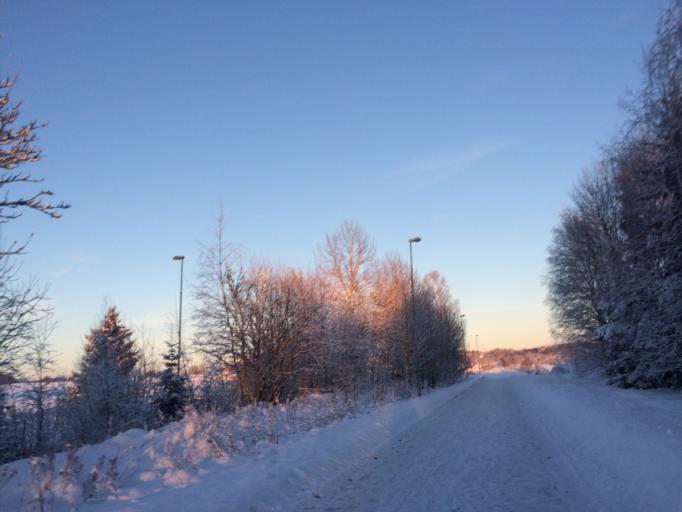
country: NO
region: Akershus
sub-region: Ski
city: Ski
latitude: 59.6917
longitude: 10.8224
